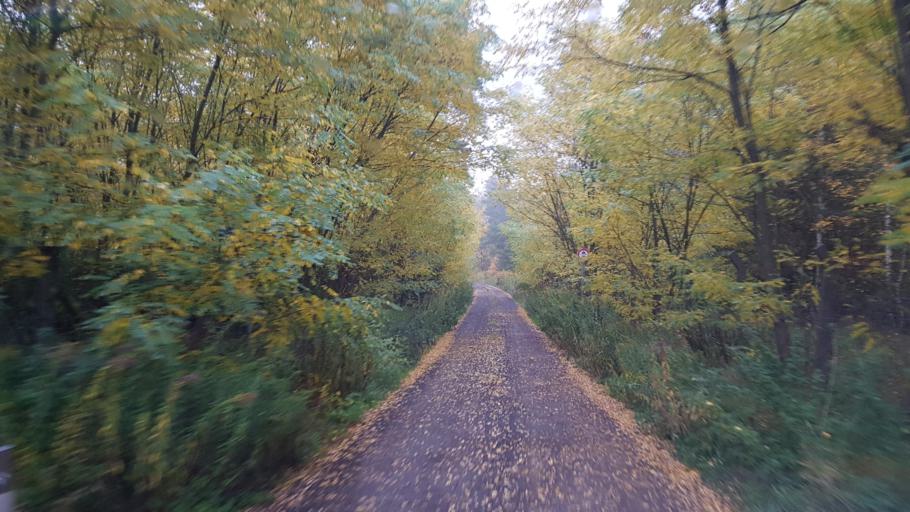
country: DE
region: Brandenburg
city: Schlieben
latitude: 51.7402
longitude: 13.3889
